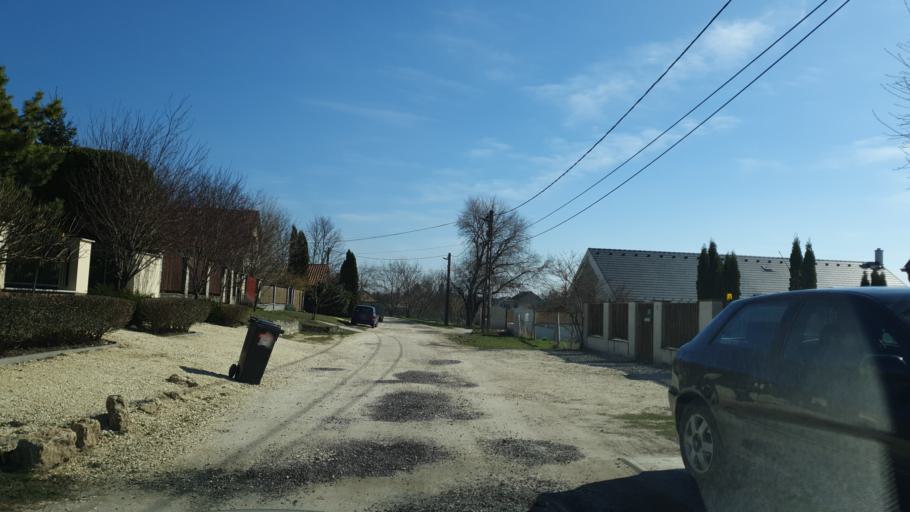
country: HU
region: Fejer
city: Etyek
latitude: 47.4514
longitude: 18.7442
